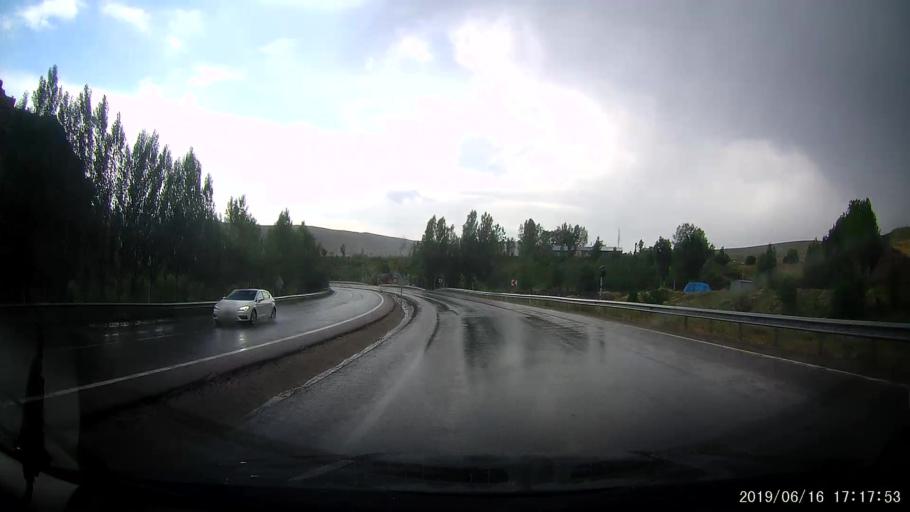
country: TR
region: Erzincan
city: Tercan
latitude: 39.8211
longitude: 40.5299
